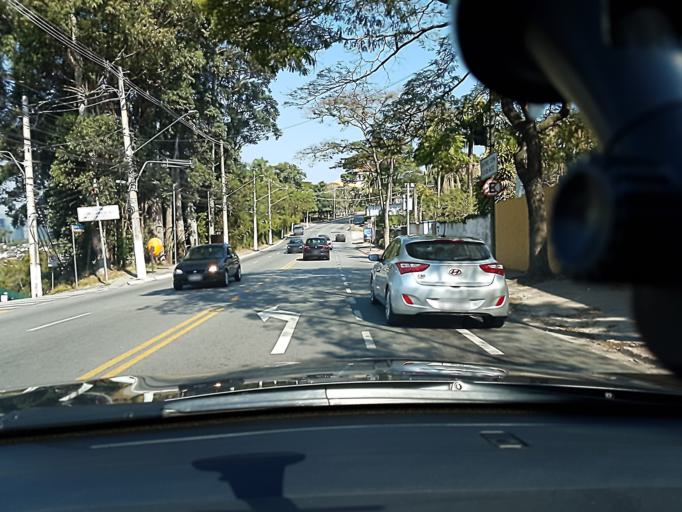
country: BR
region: Sao Paulo
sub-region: Taboao Da Serra
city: Taboao da Serra
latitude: -23.6071
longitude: -46.7125
